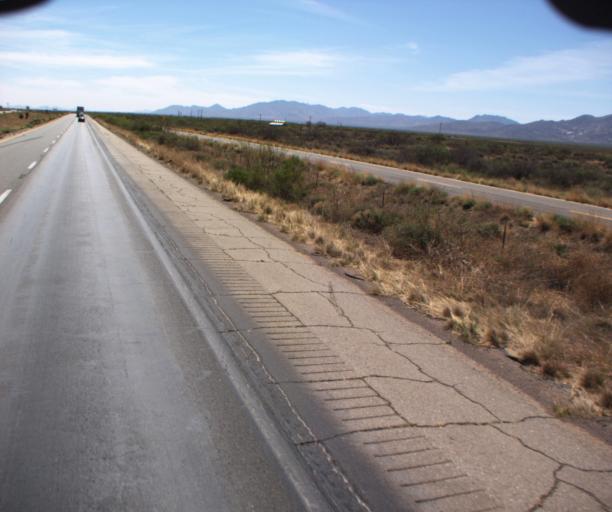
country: US
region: Arizona
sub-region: Cochise County
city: Willcox
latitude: 32.3245
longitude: -109.5054
